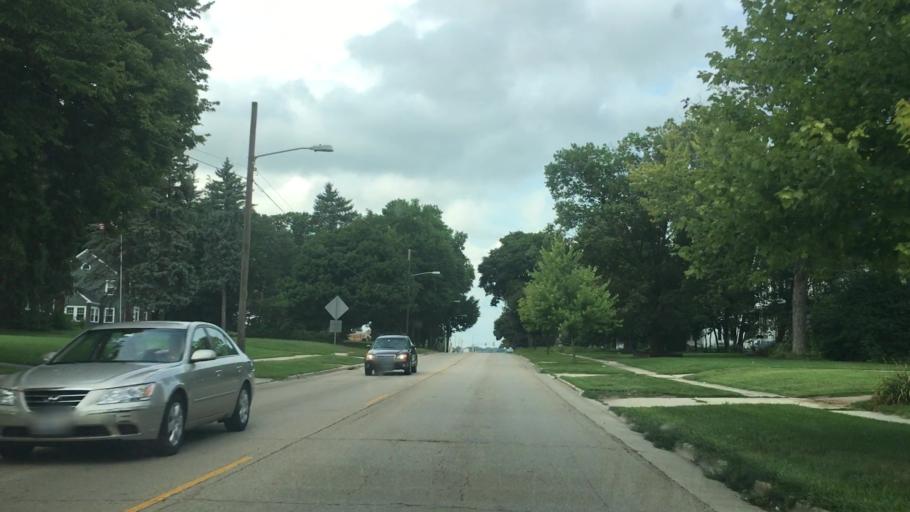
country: US
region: Illinois
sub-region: Ogle County
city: Rochelle
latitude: 41.9302
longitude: -89.0684
